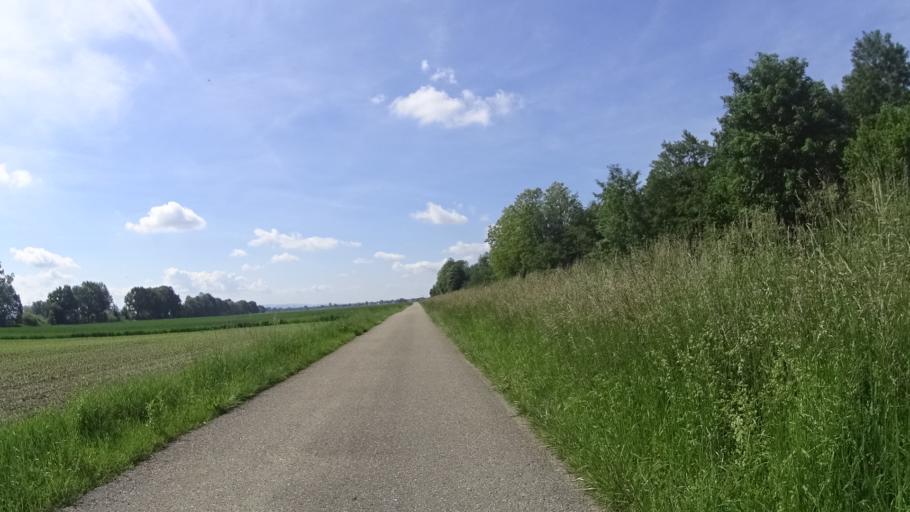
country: DE
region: Baden-Wuerttemberg
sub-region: Freiburg Region
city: Schutterwald
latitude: 48.4865
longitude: 7.8178
